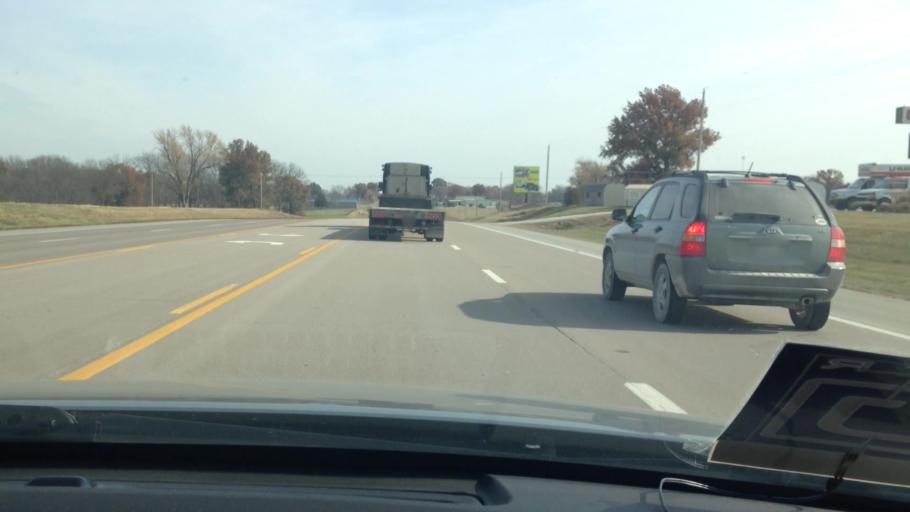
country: US
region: Missouri
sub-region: Henry County
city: Clinton
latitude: 38.3898
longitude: -93.8183
